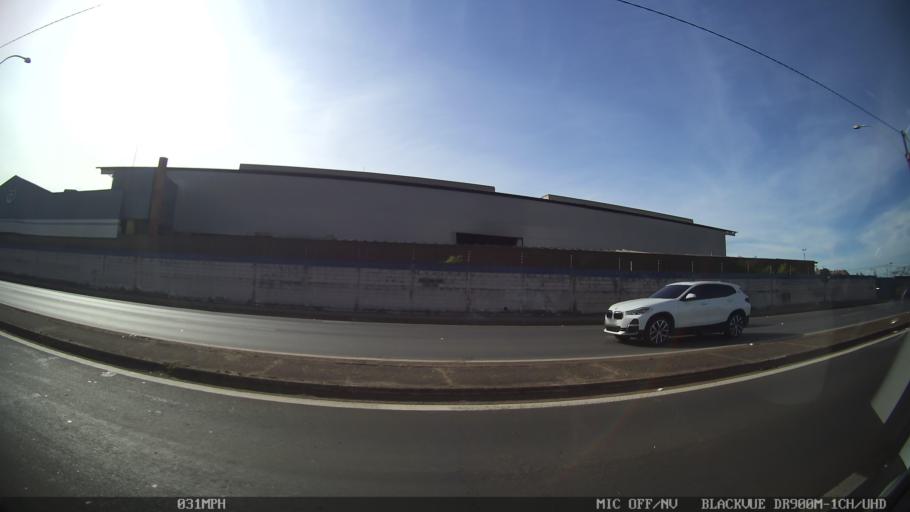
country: BR
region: Sao Paulo
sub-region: Piracicaba
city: Piracicaba
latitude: -22.7610
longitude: -47.6452
